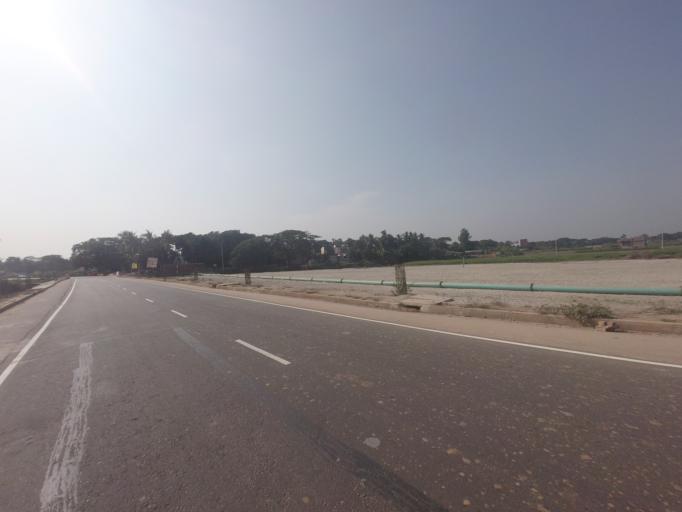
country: BD
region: Dhaka
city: Azimpur
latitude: 23.7340
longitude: 90.3242
